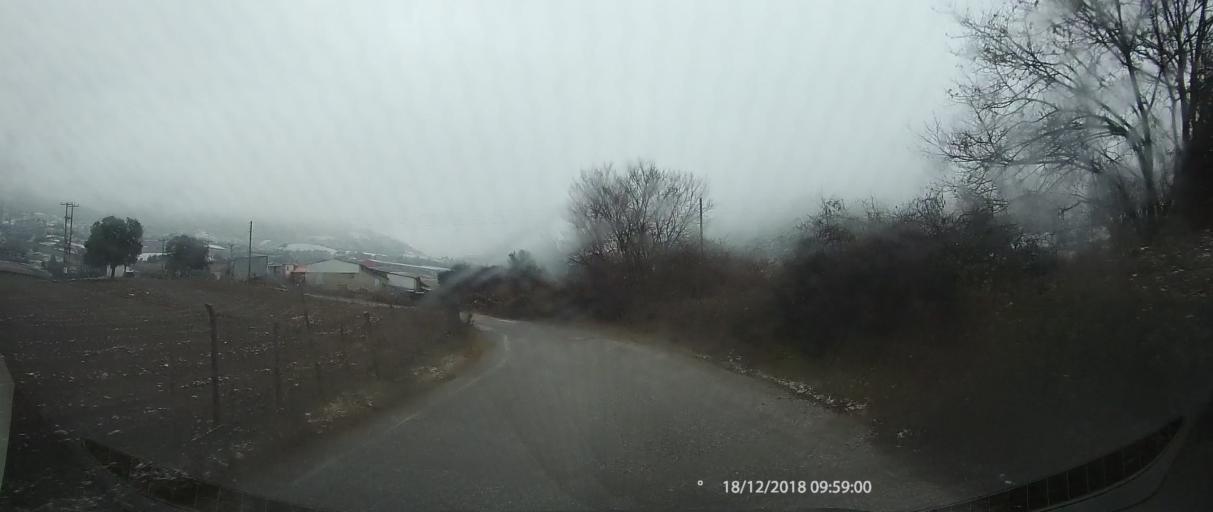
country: GR
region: Thessaly
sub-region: Nomos Larisis
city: Livadi
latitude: 40.0303
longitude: 22.2432
